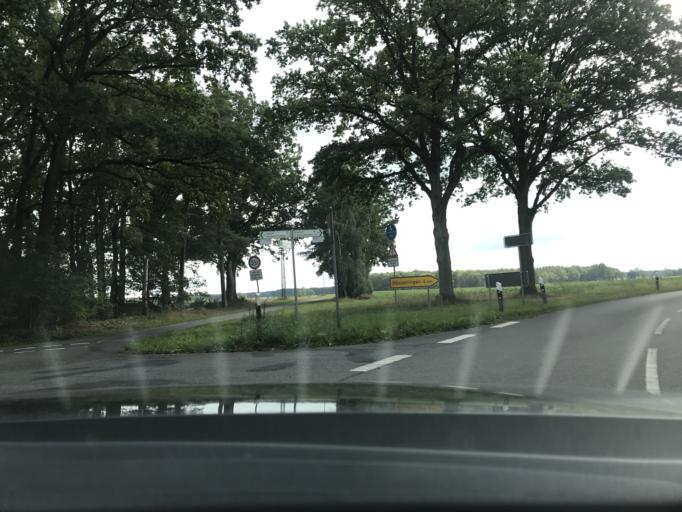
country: DE
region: Lower Saxony
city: Suderburg
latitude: 52.8839
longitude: 10.4431
